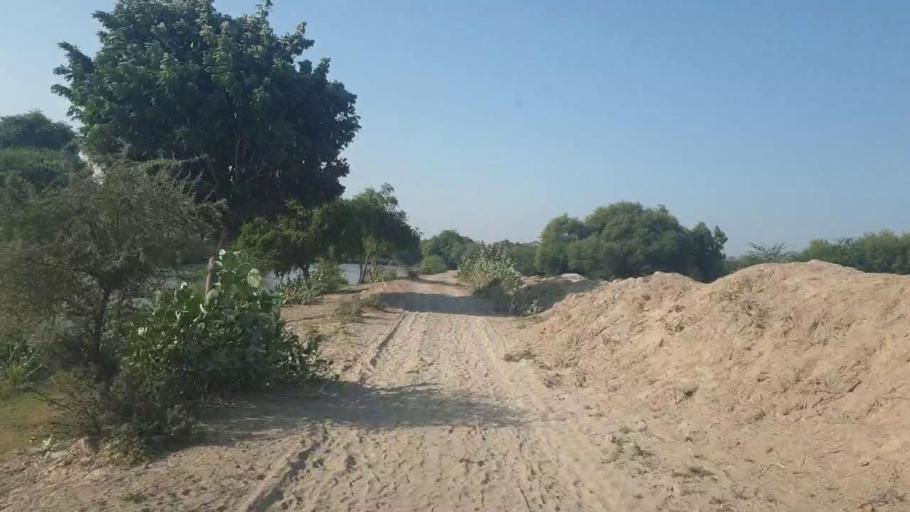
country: PK
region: Sindh
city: Tando Bago
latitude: 24.7193
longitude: 68.9162
